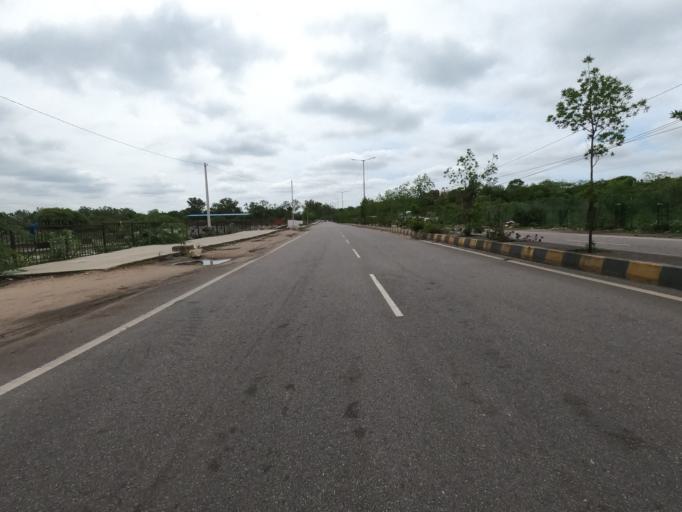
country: IN
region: Telangana
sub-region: Hyderabad
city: Hyderabad
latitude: 17.3199
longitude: 78.3897
